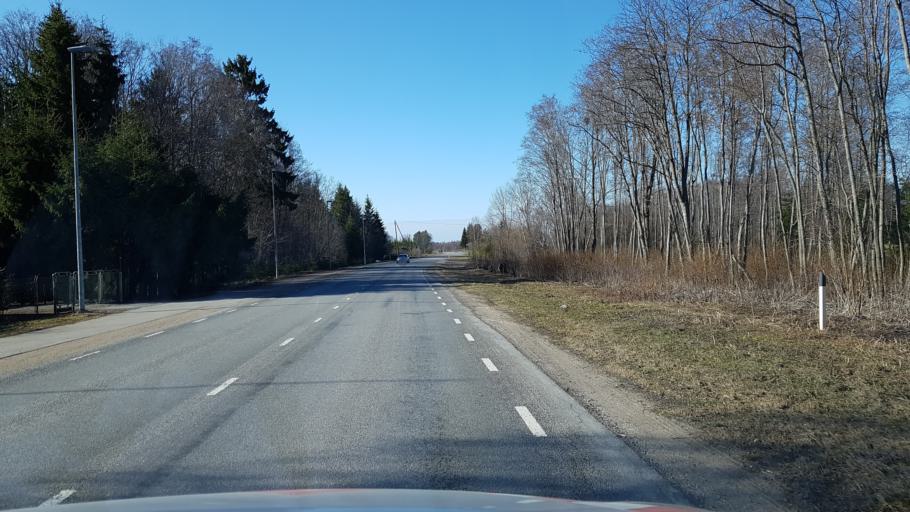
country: EE
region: Laeaene-Virumaa
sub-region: Haljala vald
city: Haljala
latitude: 59.4436
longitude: 26.2543
